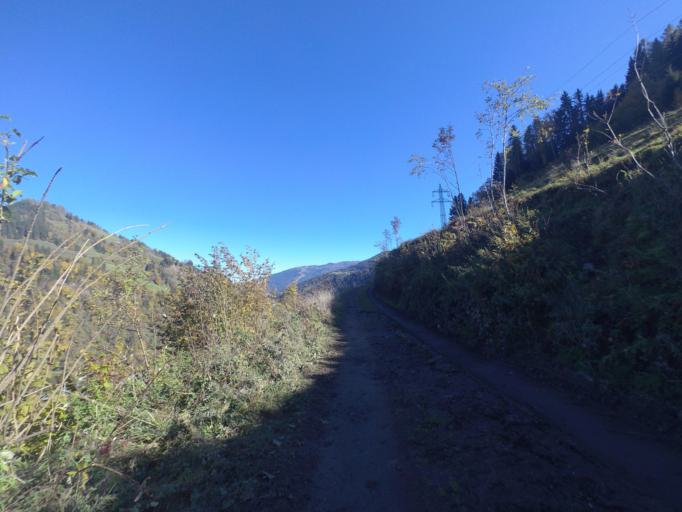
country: AT
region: Salzburg
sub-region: Politischer Bezirk Sankt Johann im Pongau
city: Sankt Johann im Pongau
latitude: 47.3317
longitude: 13.2118
